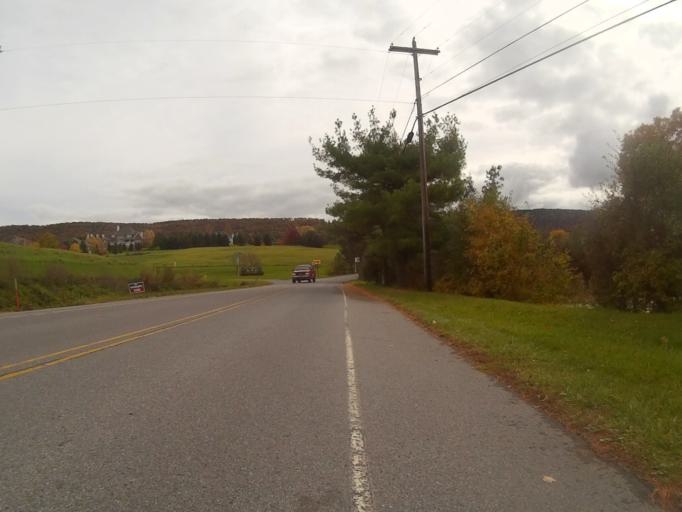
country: US
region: Pennsylvania
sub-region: Centre County
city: Boalsburg
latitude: 40.7781
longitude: -77.7582
